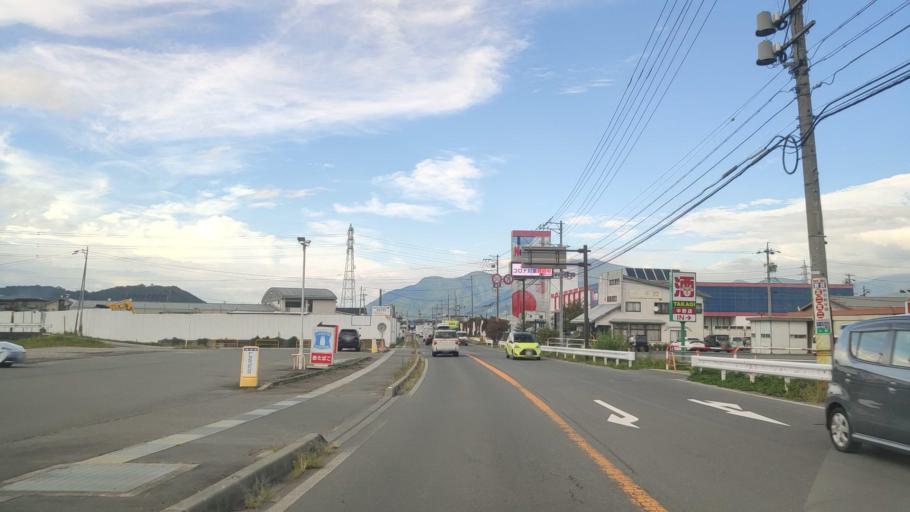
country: JP
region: Nagano
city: Nakano
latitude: 36.7308
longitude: 138.3421
